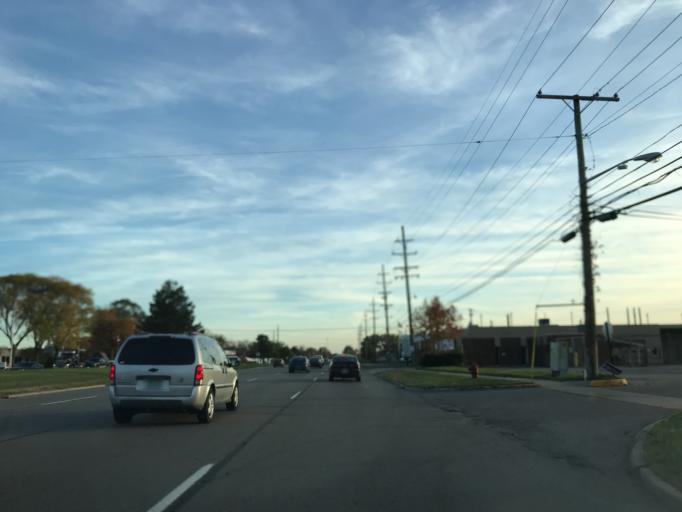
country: US
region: Michigan
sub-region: Oakland County
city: Southfield
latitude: 42.4478
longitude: -83.2785
